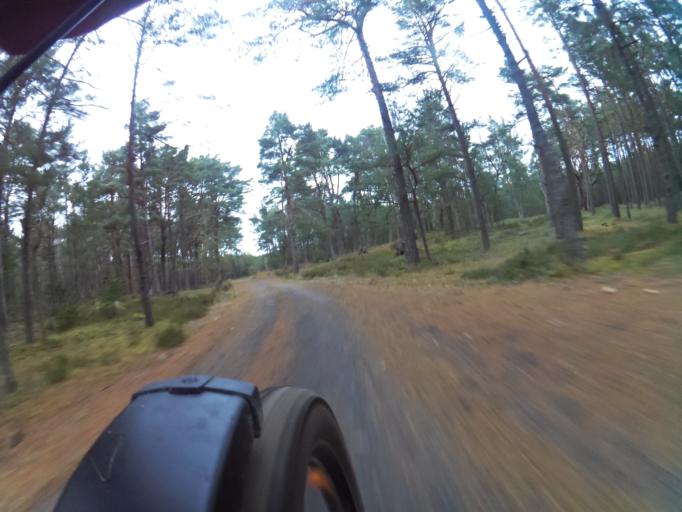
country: PL
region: Pomeranian Voivodeship
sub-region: Powiat wejherowski
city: Choczewo
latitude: 54.7857
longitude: 17.7467
